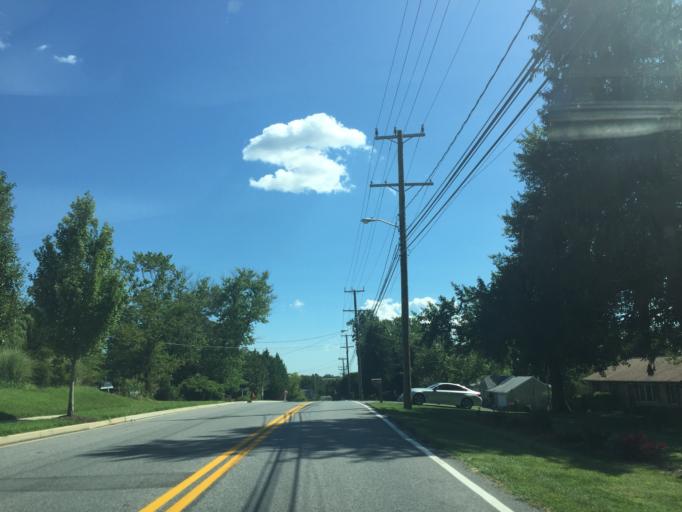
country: US
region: Maryland
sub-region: Baltimore County
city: White Marsh
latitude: 39.3957
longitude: -76.4415
